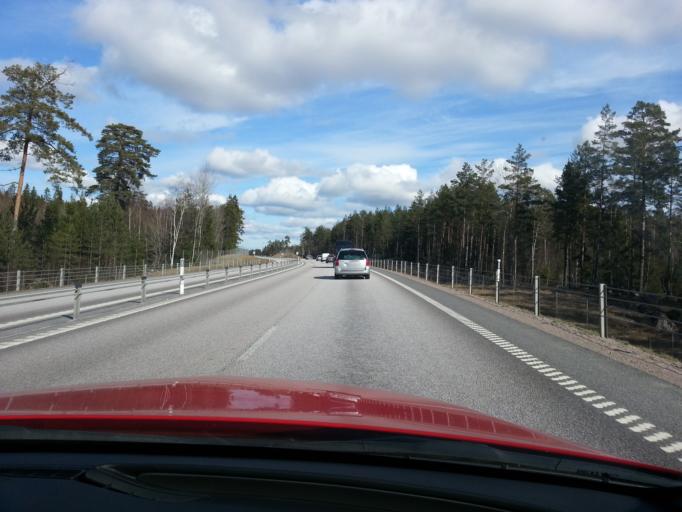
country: SE
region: Uppsala
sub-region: Uppsala Kommun
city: Storvreta
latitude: 59.9285
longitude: 17.7955
